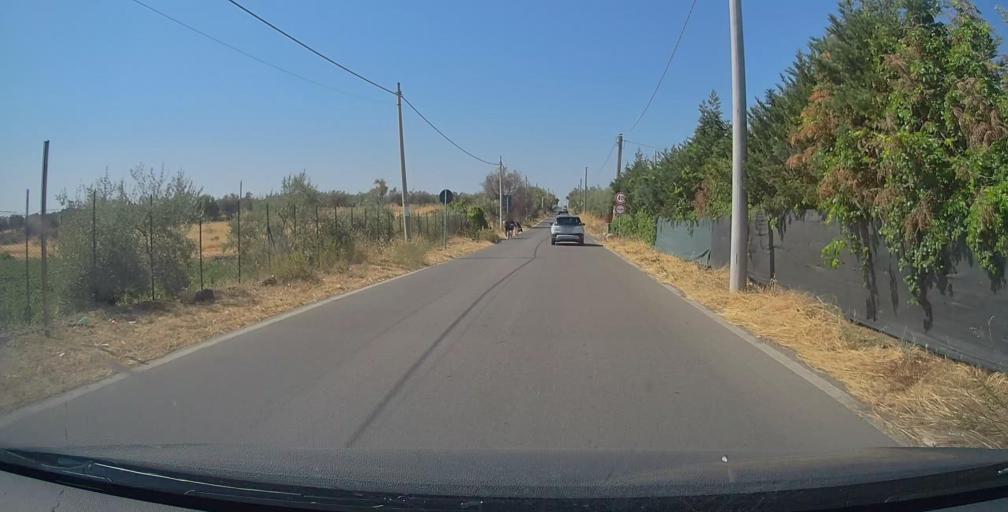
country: IT
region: Sicily
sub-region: Catania
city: Palazzolo
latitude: 37.5454
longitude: 14.9304
